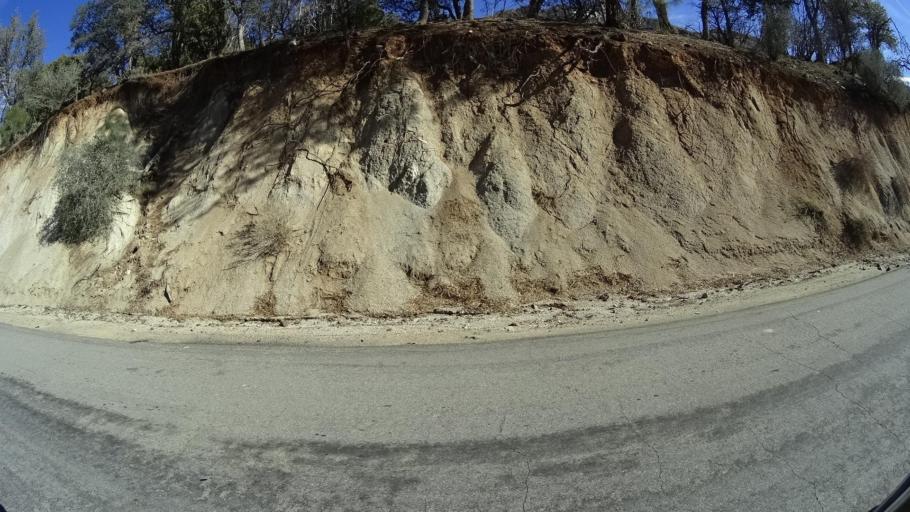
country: US
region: California
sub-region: Kern County
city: Bodfish
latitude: 35.5534
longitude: -118.5066
